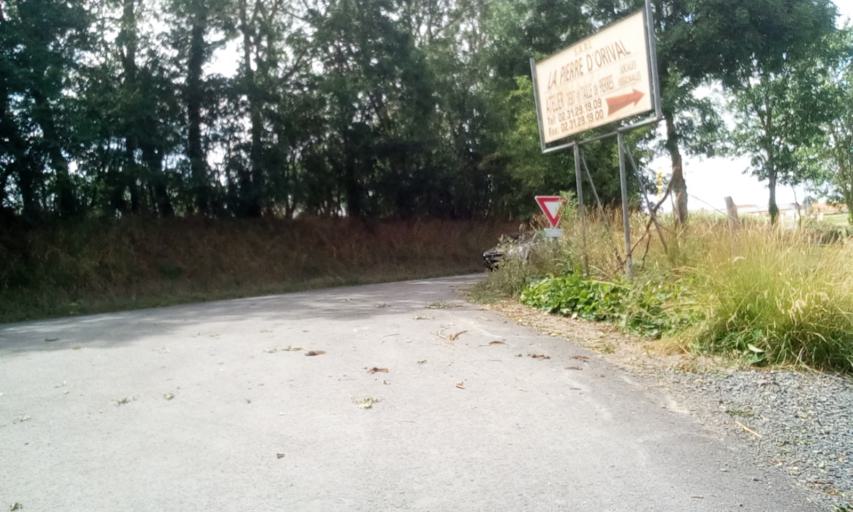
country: FR
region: Lower Normandy
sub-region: Departement du Calvados
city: Creully
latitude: 49.2824
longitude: -0.5271
